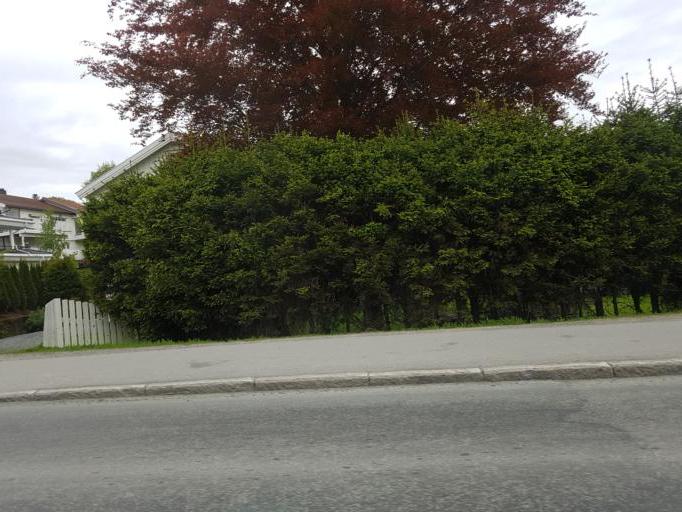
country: NO
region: Nord-Trondelag
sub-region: Levanger
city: Levanger
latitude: 63.7470
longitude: 11.2923
